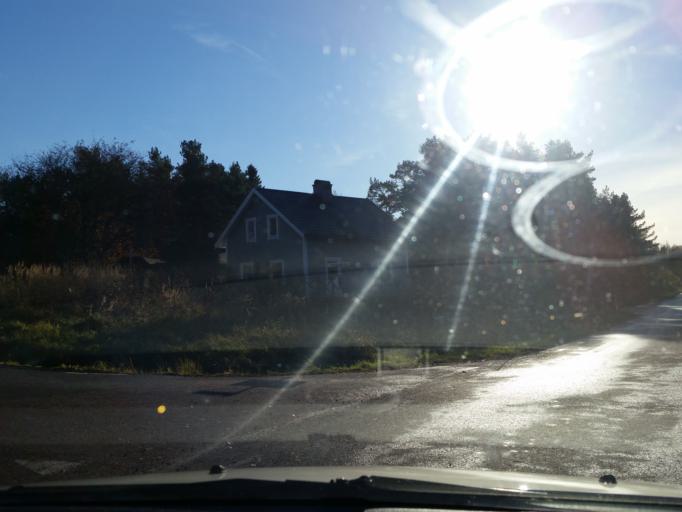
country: AX
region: Alands landsbygd
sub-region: Jomala
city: Jomala
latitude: 60.2012
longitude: 19.9570
